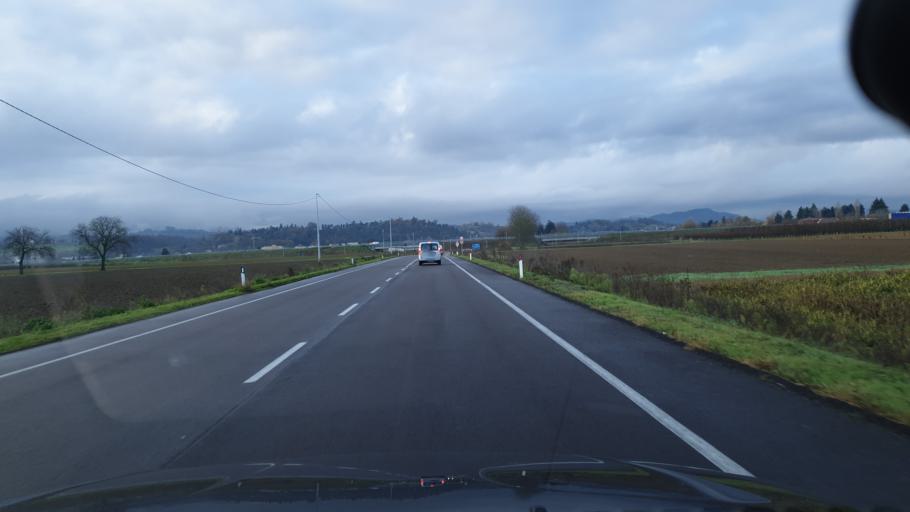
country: IT
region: Emilia-Romagna
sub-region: Provincia di Bologna
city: Crespellano
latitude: 44.5228
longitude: 11.1415
